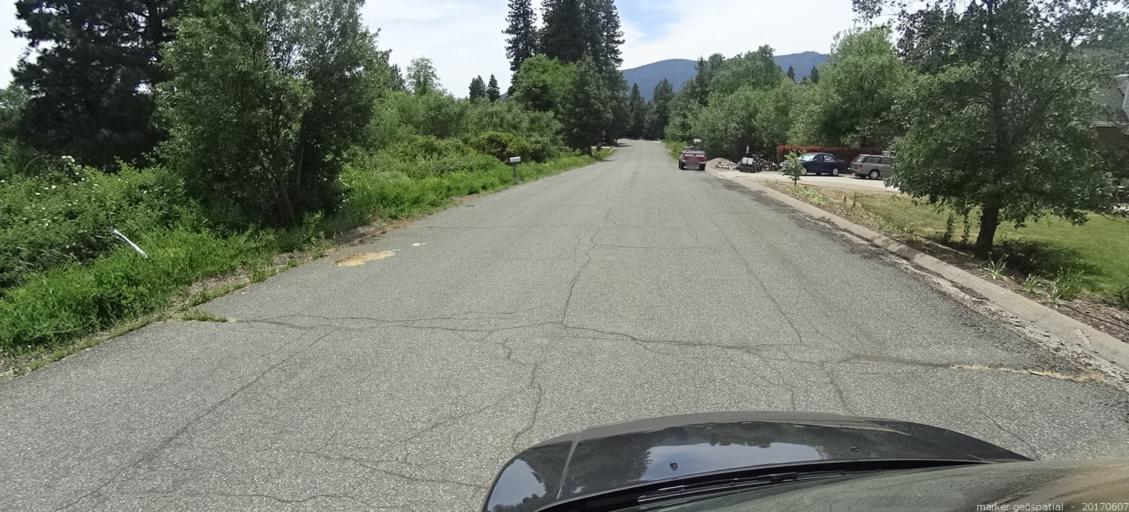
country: US
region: California
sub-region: Siskiyou County
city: Mount Shasta
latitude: 41.2979
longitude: -122.3213
